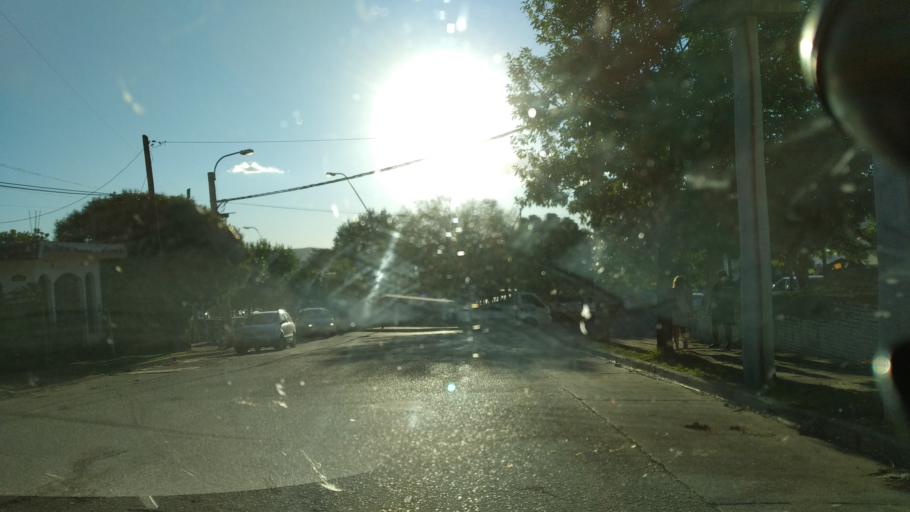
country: AR
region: Cordoba
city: Mina Clavero
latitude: -31.7208
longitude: -65.0033
